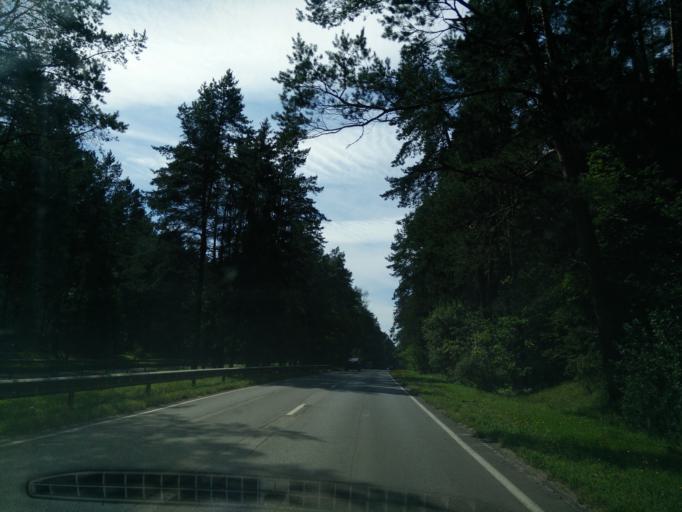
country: LT
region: Vilnius County
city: Rasos
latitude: 54.7466
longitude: 25.3558
